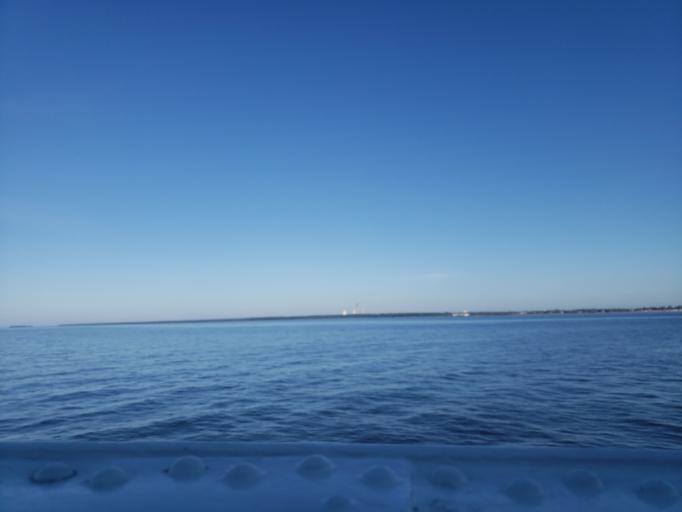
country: RU
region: St.-Petersburg
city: Lakhtinskiy
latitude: 59.9583
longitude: 30.1683
